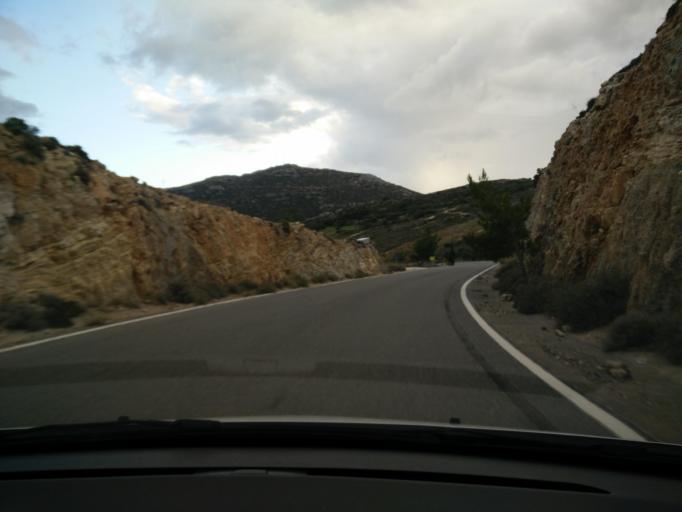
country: GR
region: Crete
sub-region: Nomos Lasithiou
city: Gra Liyia
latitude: 35.0872
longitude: 25.7061
